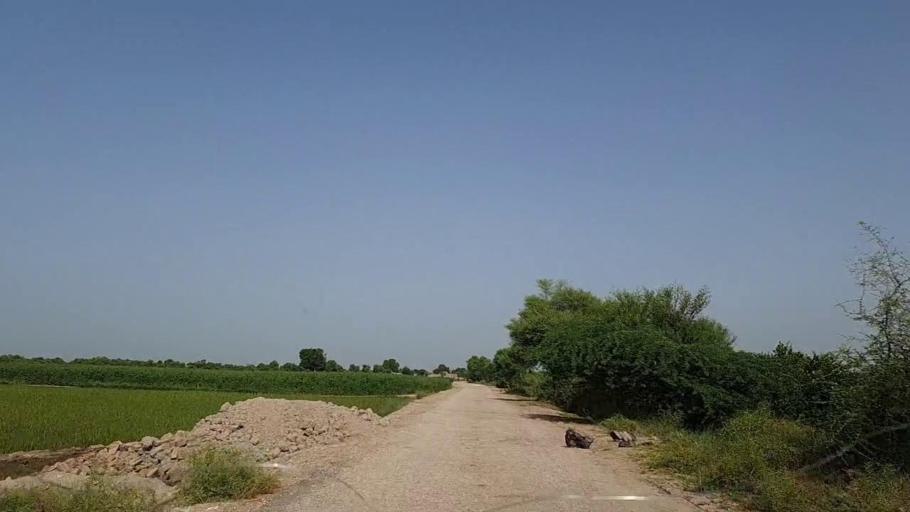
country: PK
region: Sindh
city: Kandiaro
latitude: 27.0719
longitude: 68.1521
